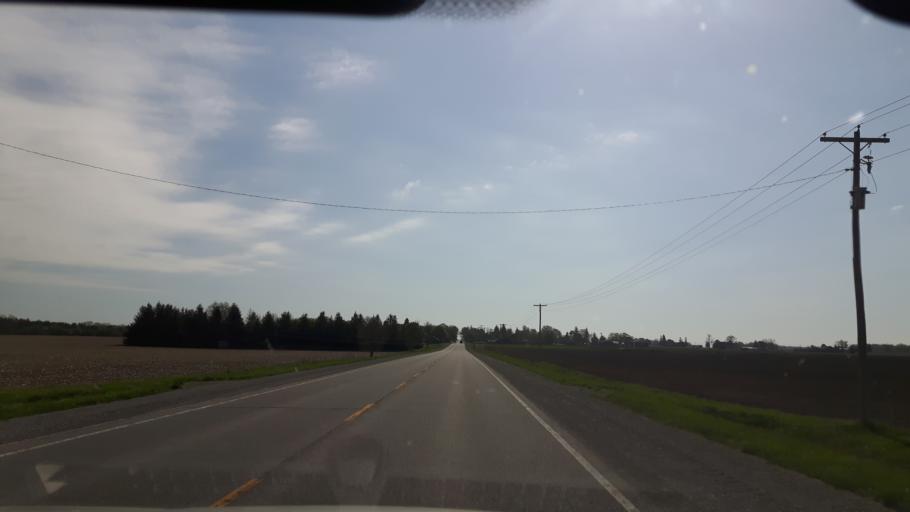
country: CA
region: Ontario
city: Bluewater
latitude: 43.5242
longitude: -81.5303
